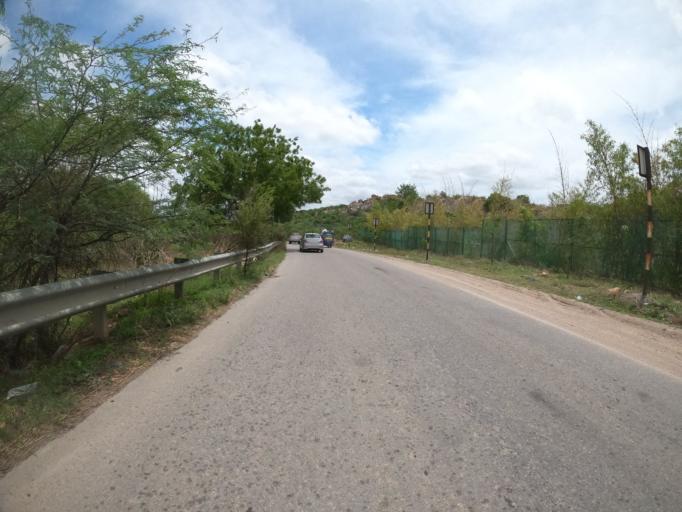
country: IN
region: Telangana
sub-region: Hyderabad
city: Hyderabad
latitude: 17.3148
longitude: 78.3722
